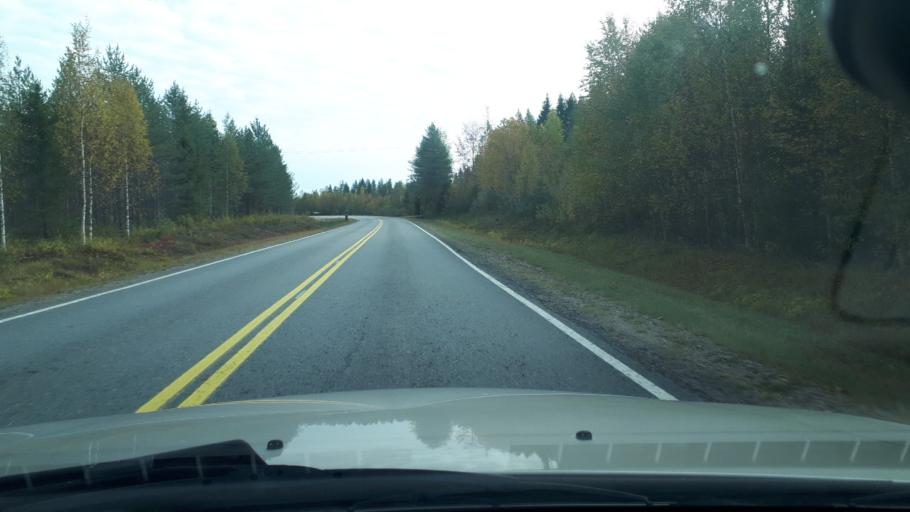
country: FI
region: Lapland
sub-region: Rovaniemi
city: Ranua
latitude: 65.9633
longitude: 25.9690
